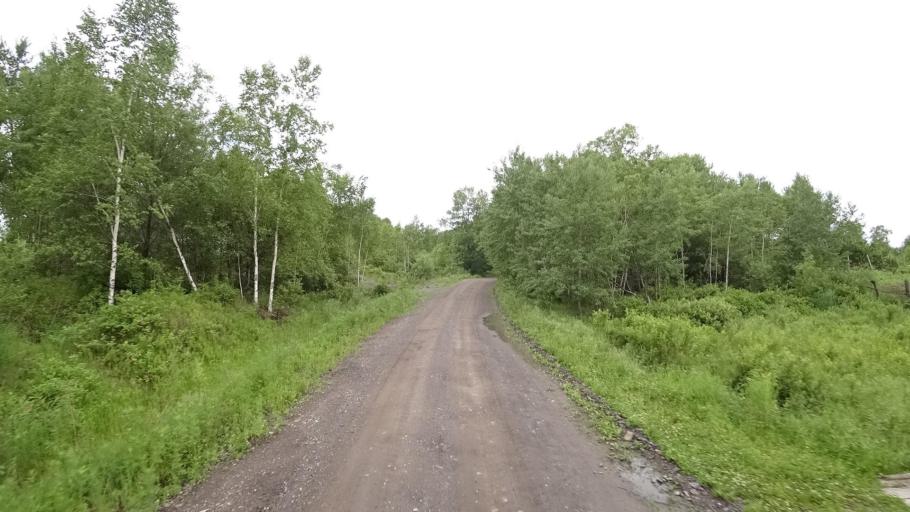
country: RU
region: Khabarovsk Krai
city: Amursk
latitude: 49.9104
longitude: 136.1563
